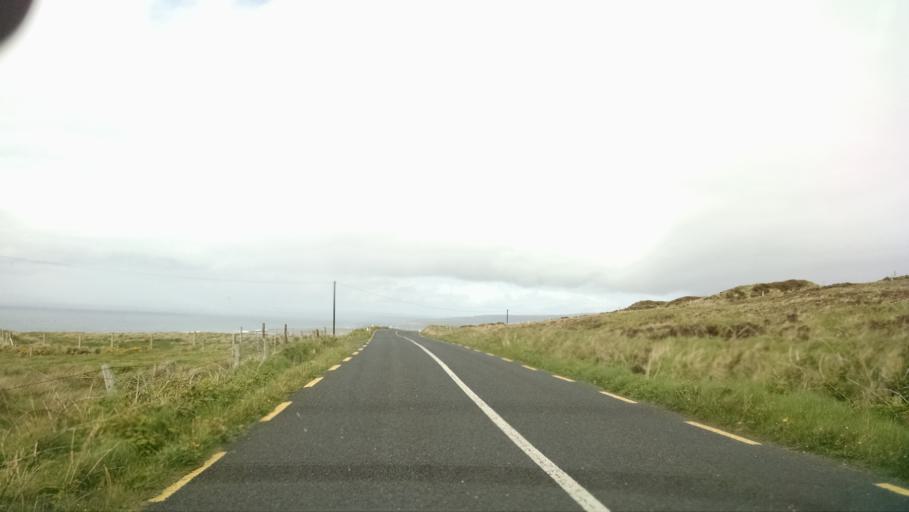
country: IE
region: Munster
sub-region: An Clar
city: Kilrush
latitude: 52.9823
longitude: -9.4187
